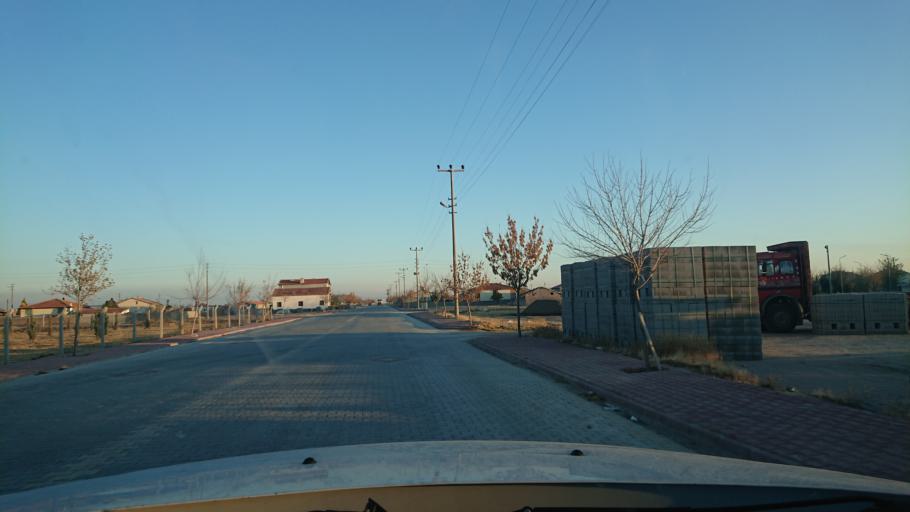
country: TR
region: Aksaray
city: Eskil
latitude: 38.3975
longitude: 33.4210
